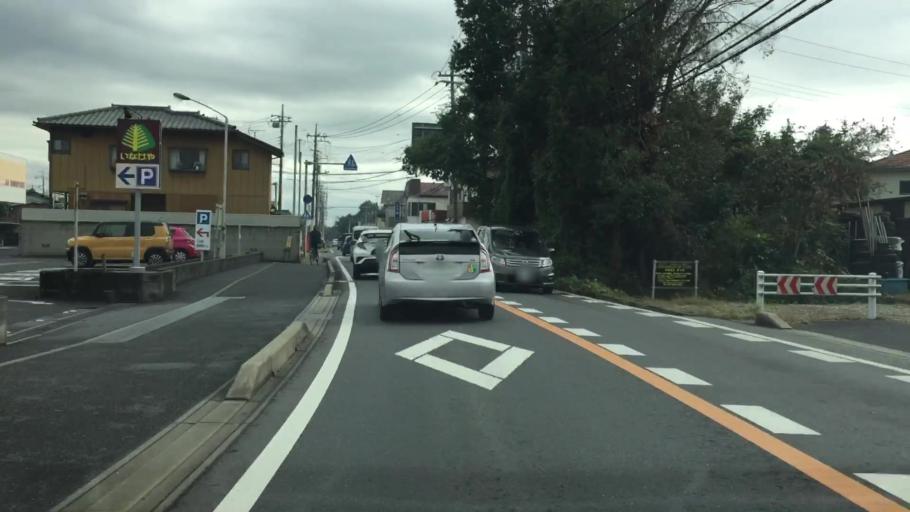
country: JP
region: Chiba
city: Abiko
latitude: 35.8426
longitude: 140.0096
